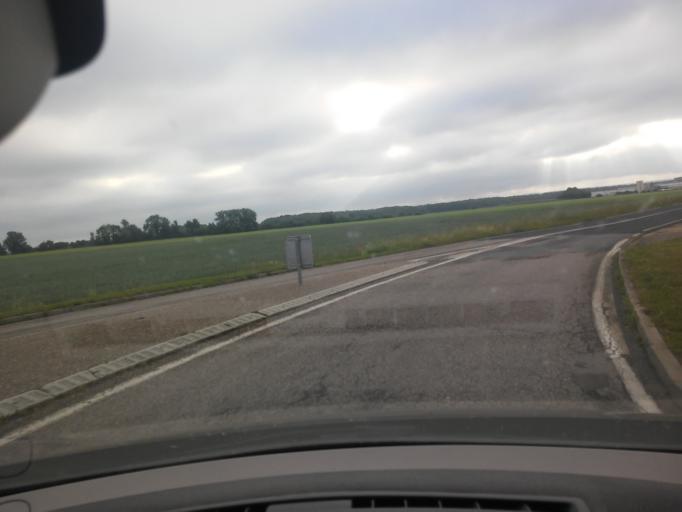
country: FR
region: Lorraine
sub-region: Departement de la Meuse
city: Vigneulles-les-Hattonchatel
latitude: 48.9787
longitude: 5.7159
